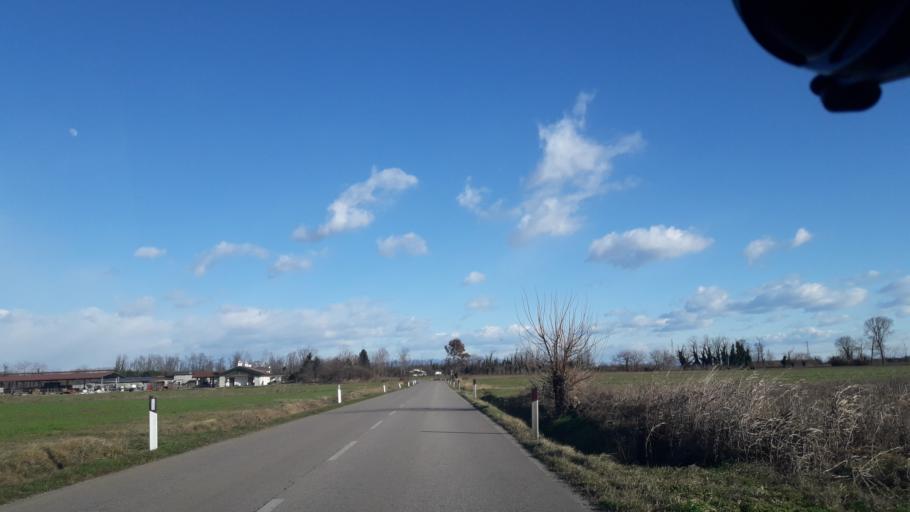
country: IT
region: Friuli Venezia Giulia
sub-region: Provincia di Udine
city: Martignacco
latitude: 46.0750
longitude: 13.1595
